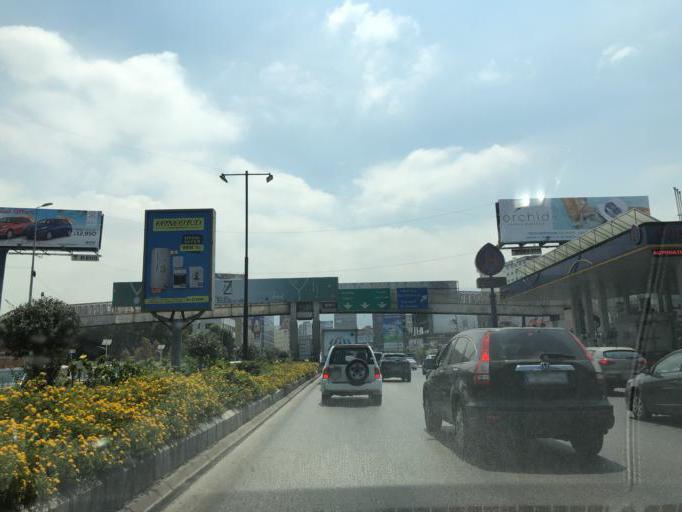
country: LB
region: Mont-Liban
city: Jdaidet el Matn
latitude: 33.8949
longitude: 35.5458
